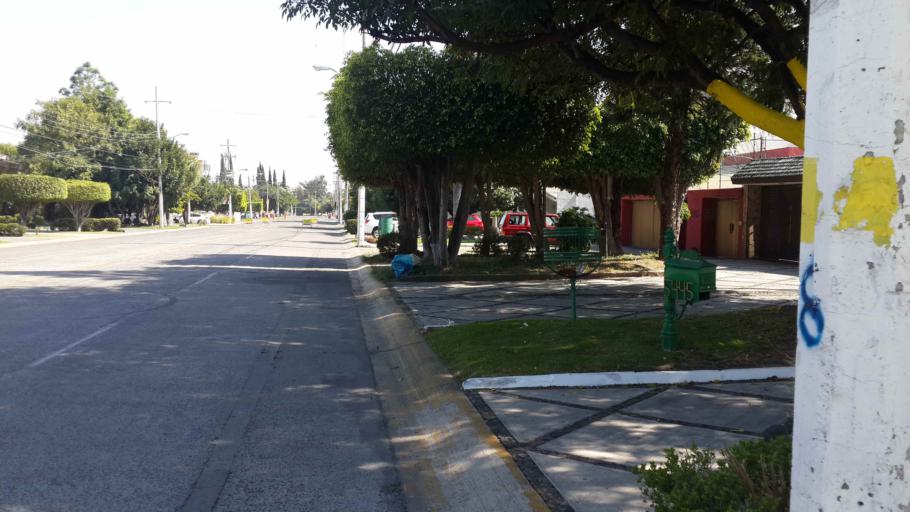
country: MX
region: Jalisco
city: Guadalajara
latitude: 20.6695
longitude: -103.4307
